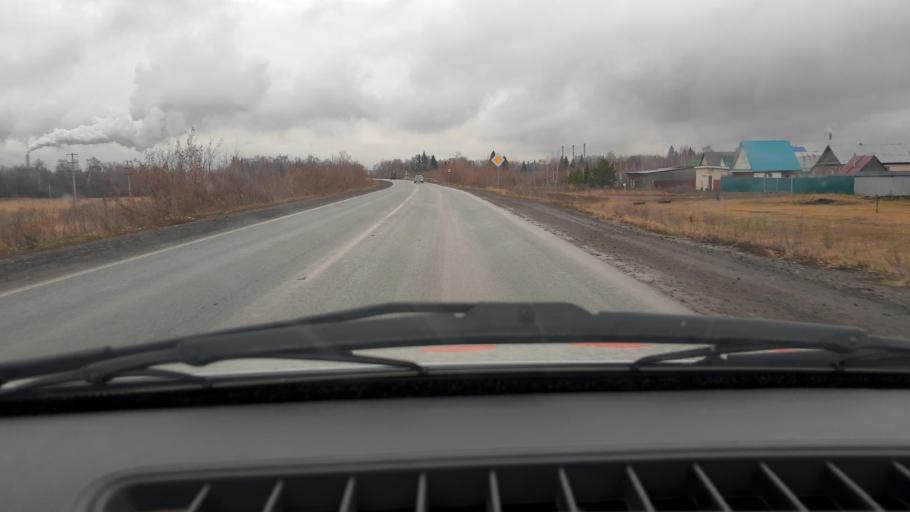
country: RU
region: Bashkortostan
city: Iglino
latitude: 54.7793
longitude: 56.2536
